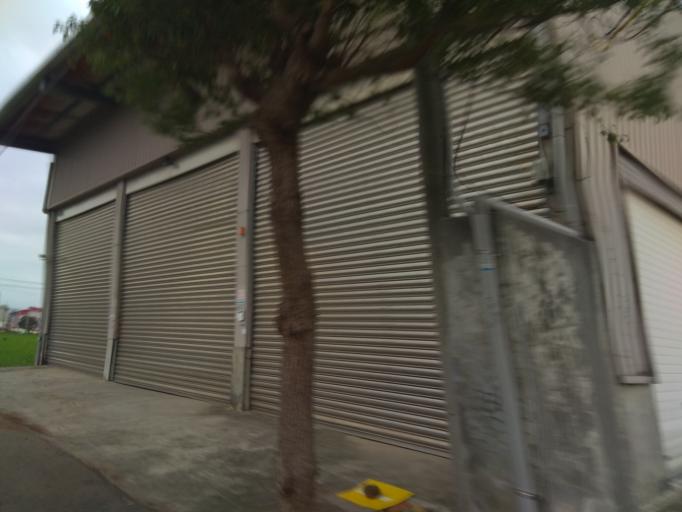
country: TW
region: Taiwan
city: Taoyuan City
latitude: 25.0358
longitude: 121.2188
